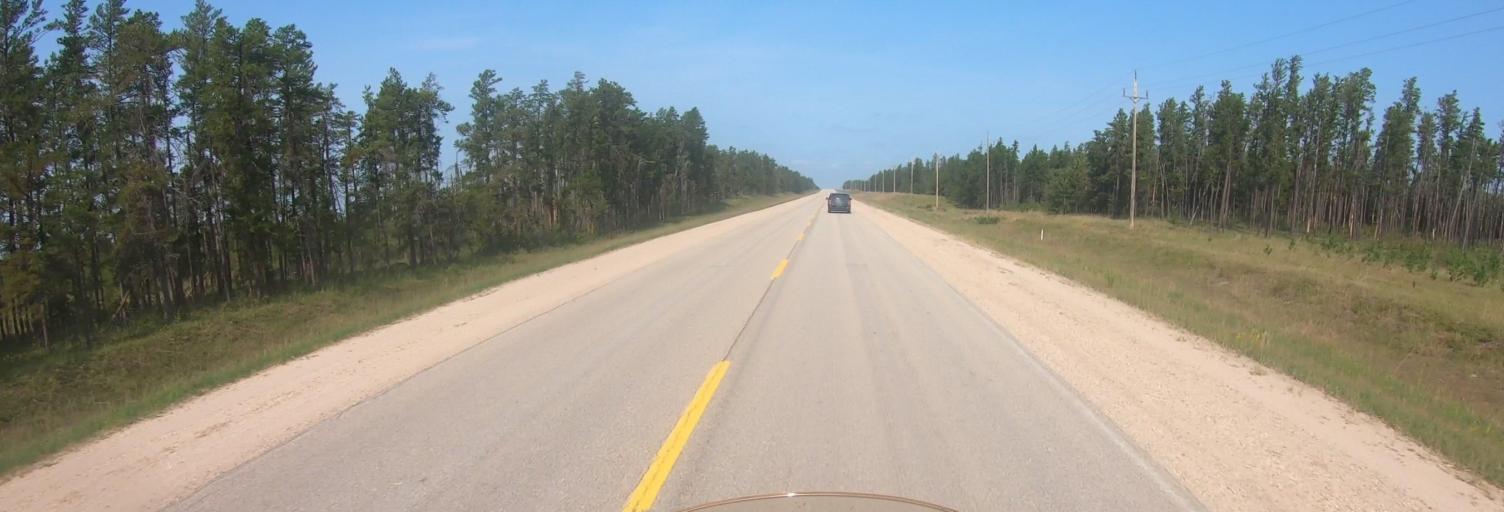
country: US
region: Minnesota
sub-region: Roseau County
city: Roseau
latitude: 49.1272
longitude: -96.0722
